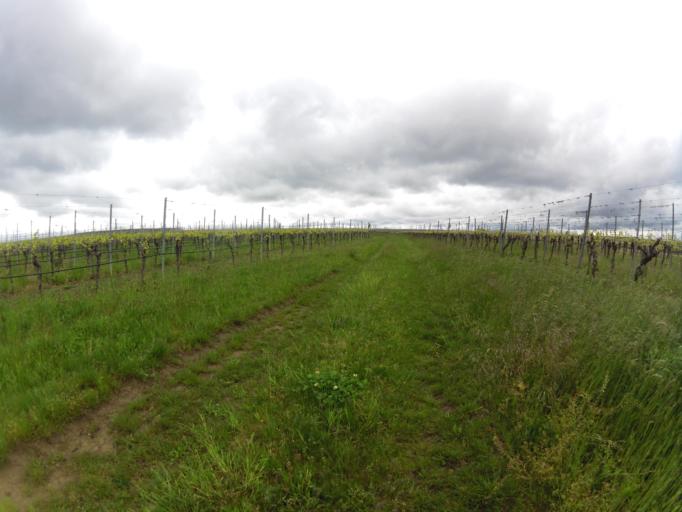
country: DE
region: Bavaria
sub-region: Regierungsbezirk Unterfranken
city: Sommerach
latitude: 49.8403
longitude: 10.2075
